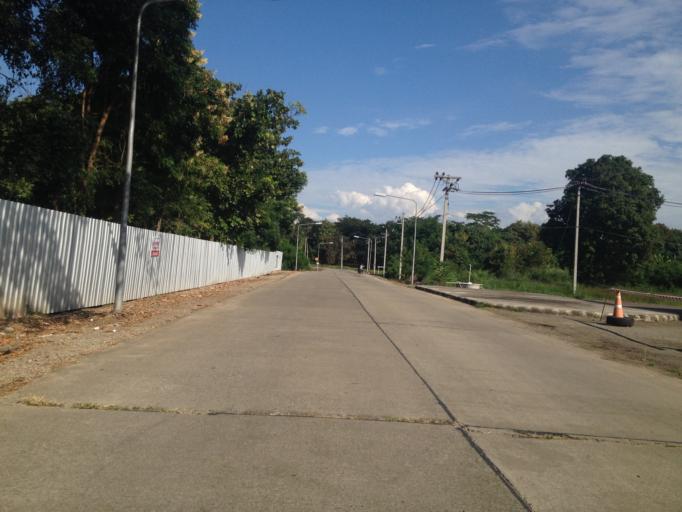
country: TH
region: Chiang Mai
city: Chiang Mai
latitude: 18.7637
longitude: 98.9373
